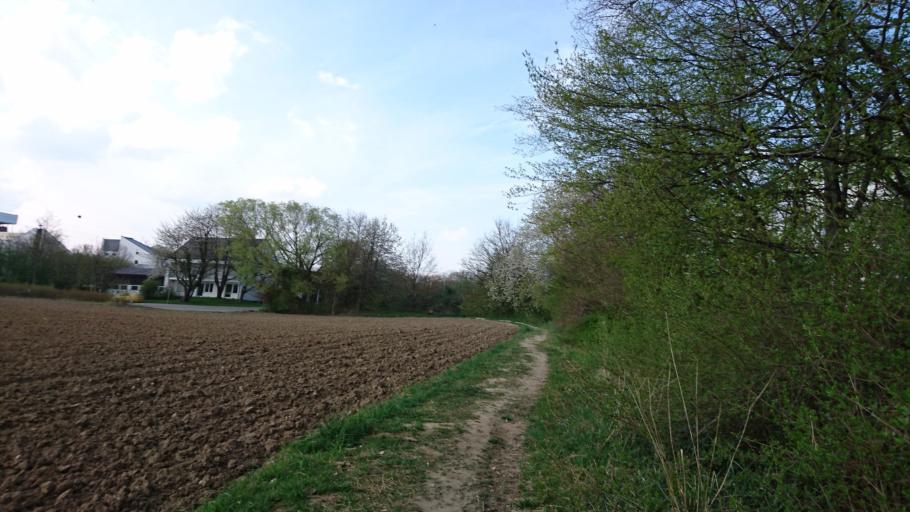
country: DE
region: Bavaria
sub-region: Swabia
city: Stadtbergen
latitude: 48.3811
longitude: 10.8457
